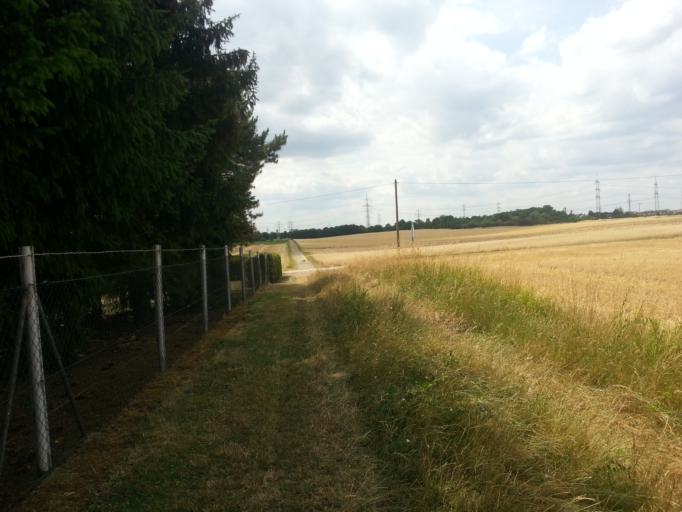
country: DE
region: Baden-Wuerttemberg
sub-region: Karlsruhe Region
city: Ilvesheim
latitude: 49.4882
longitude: 8.5693
